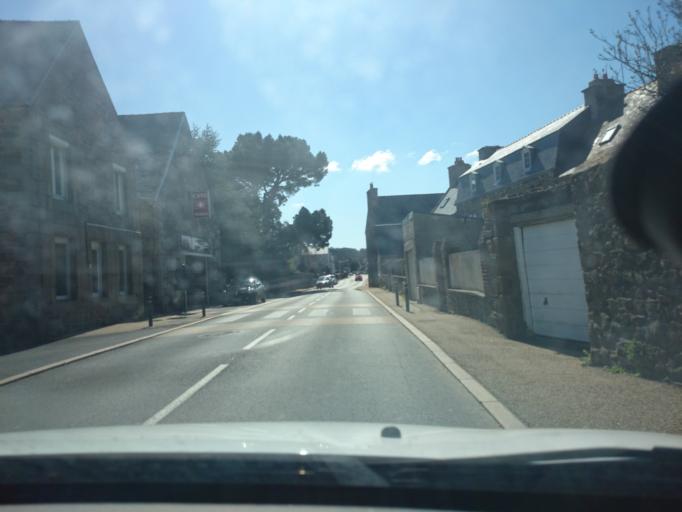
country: FR
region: Brittany
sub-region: Departement des Cotes-d'Armor
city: Perros-Guirec
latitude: 48.8006
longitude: -3.4428
